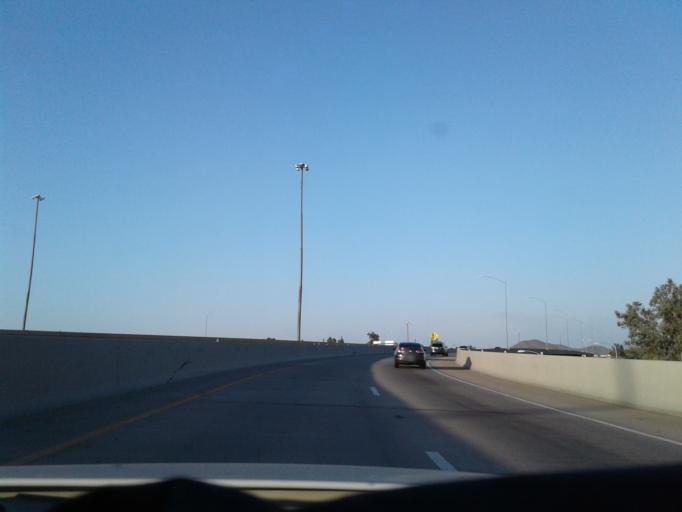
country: US
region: Arizona
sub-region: Maricopa County
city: Glendale
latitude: 33.6678
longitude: -112.1117
